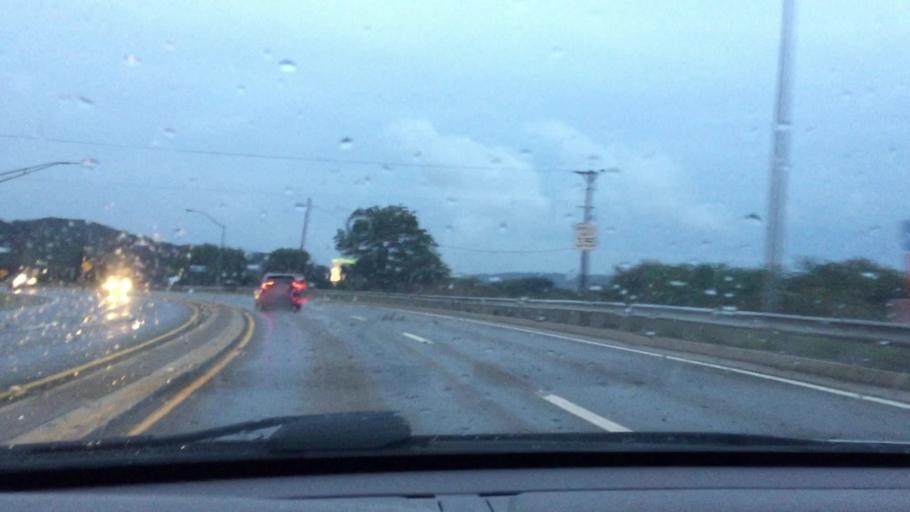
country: US
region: Pennsylvania
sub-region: Allegheny County
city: Cheswick
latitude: 40.5550
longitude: -79.8112
